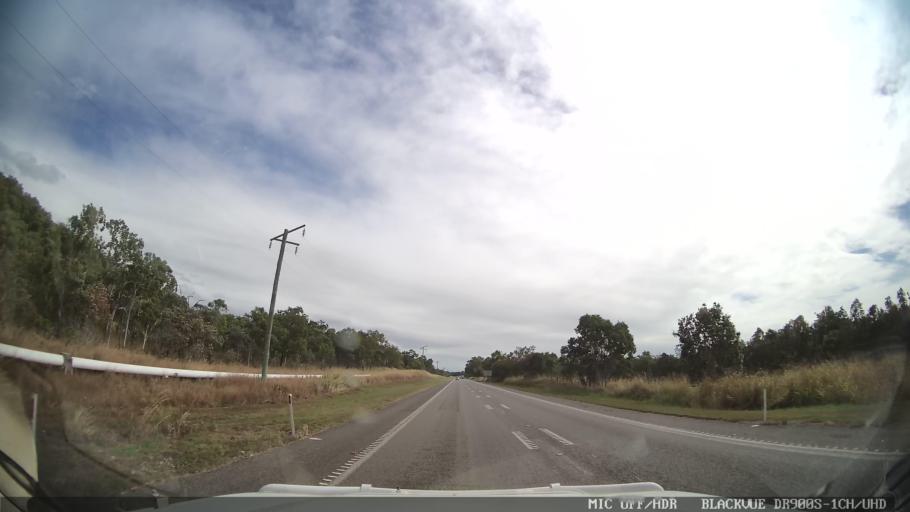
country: AU
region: Queensland
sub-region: Hinchinbrook
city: Ingham
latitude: -19.0061
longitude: 146.3600
